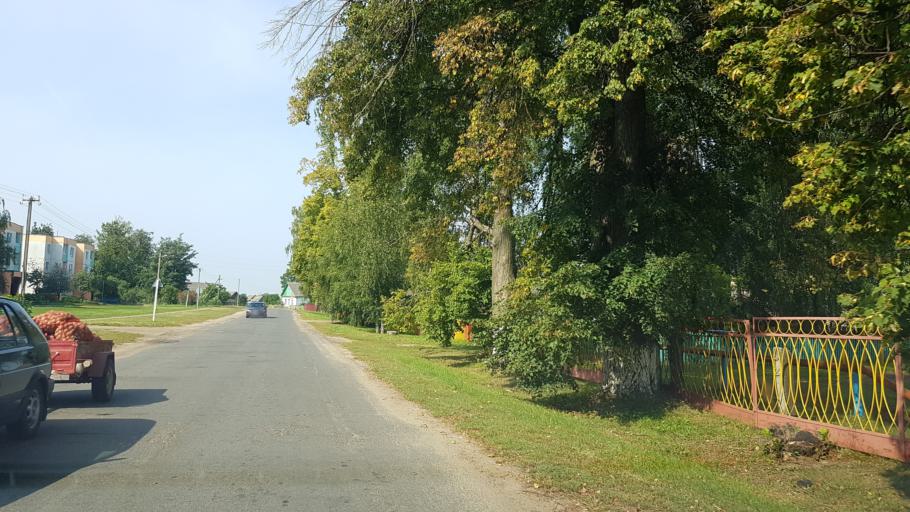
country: BY
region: Mogilev
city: Myshkavichy
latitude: 53.1608
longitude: 29.6867
